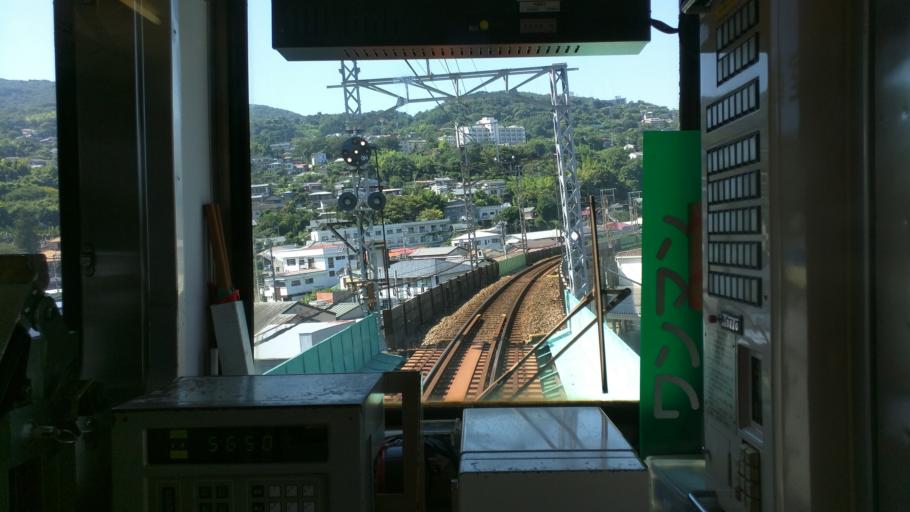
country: JP
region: Shizuoka
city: Ito
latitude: 34.9535
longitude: 139.0875
